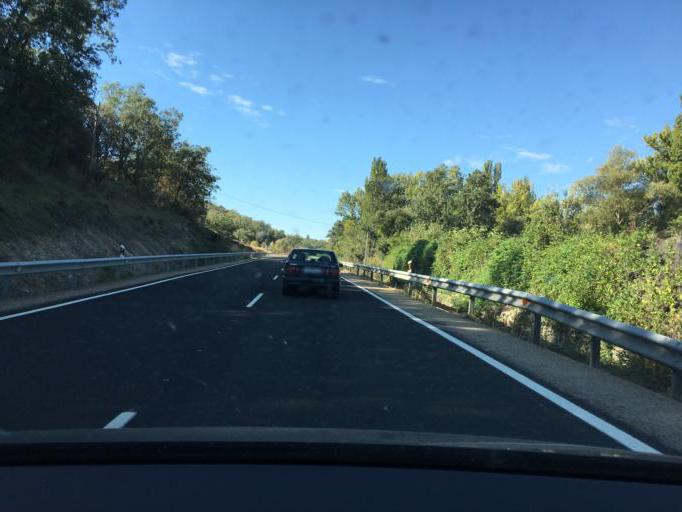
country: ES
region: Madrid
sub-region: Provincia de Madrid
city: Venturada
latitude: 40.8035
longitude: -3.6074
